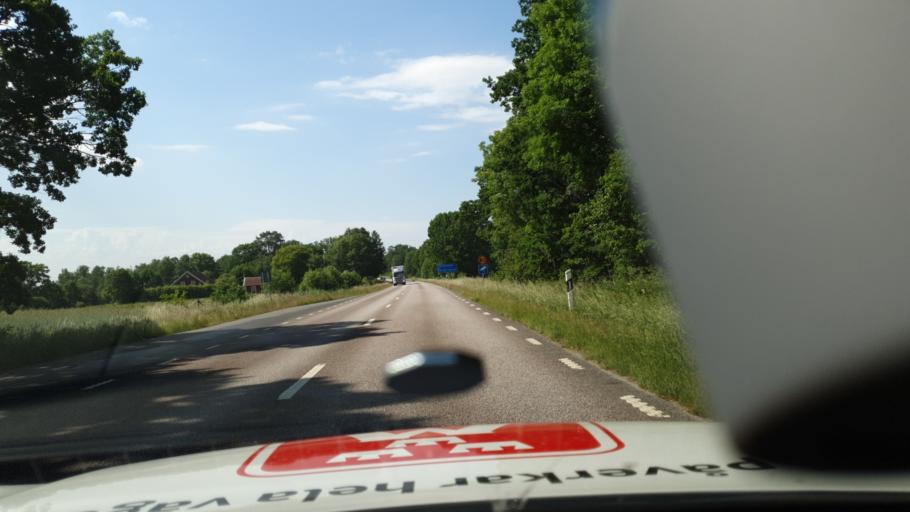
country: SE
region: Vaestra Goetaland
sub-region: Hjo Kommun
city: Hjo
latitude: 58.2300
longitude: 14.2155
